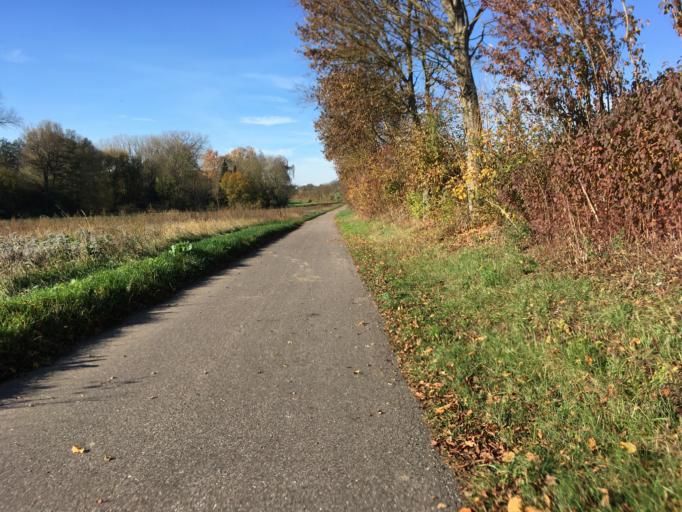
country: DE
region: Baden-Wuerttemberg
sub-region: Karlsruhe Region
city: Sulzfeld
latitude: 49.1120
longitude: 8.8469
